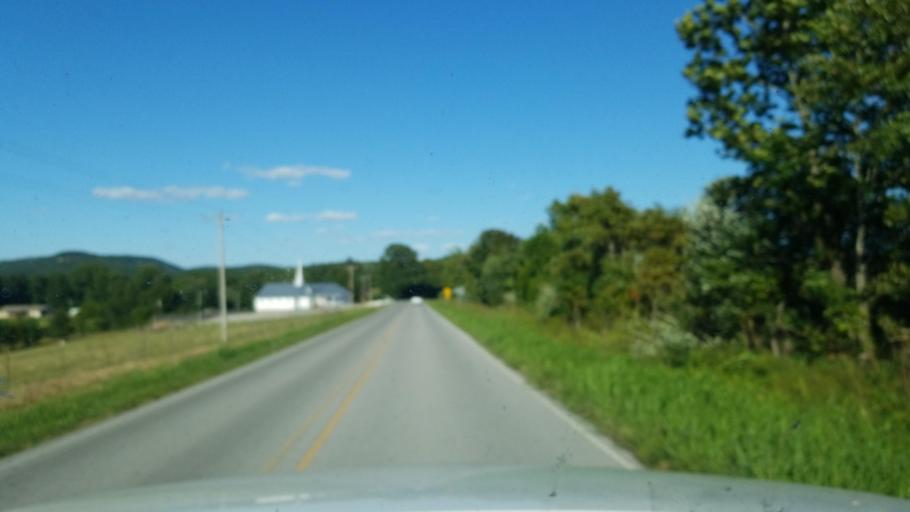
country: US
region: Illinois
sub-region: Hardin County
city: Elizabethtown
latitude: 37.5722
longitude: -88.3972
